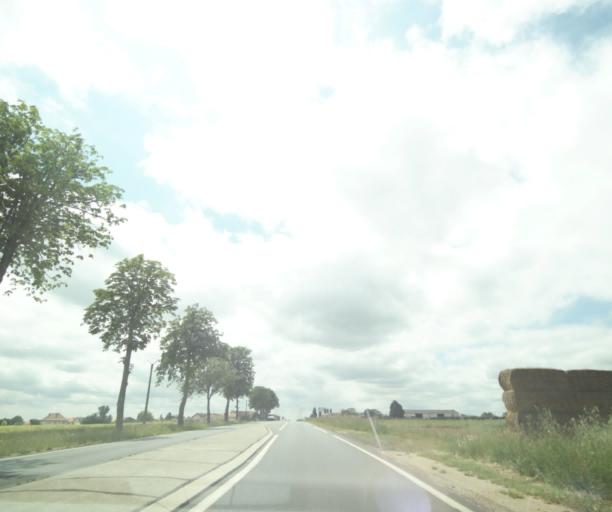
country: FR
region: Poitou-Charentes
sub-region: Departement des Deux-Sevres
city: Saint-Jean-de-Thouars
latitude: 46.9273
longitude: -0.1988
